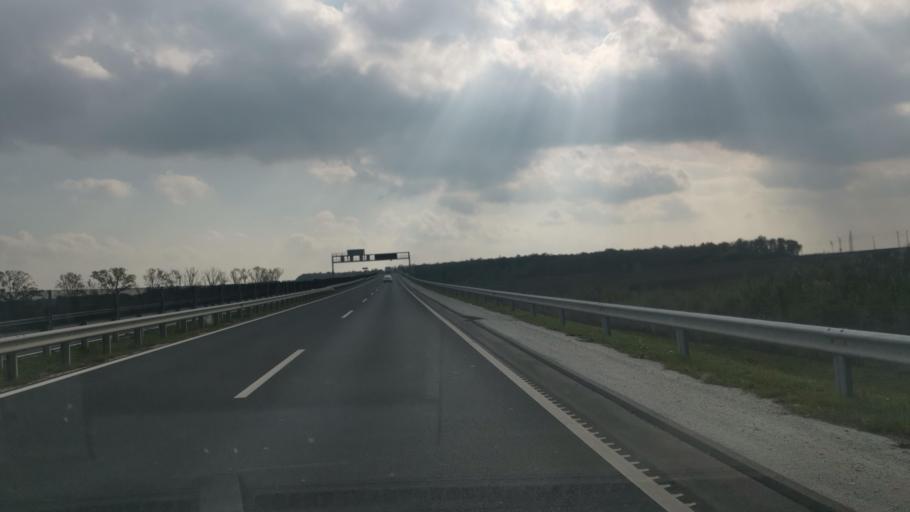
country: AT
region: Burgenland
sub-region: Politischer Bezirk Oberpullendorf
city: Deutschkreutz
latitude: 47.6395
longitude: 16.6280
